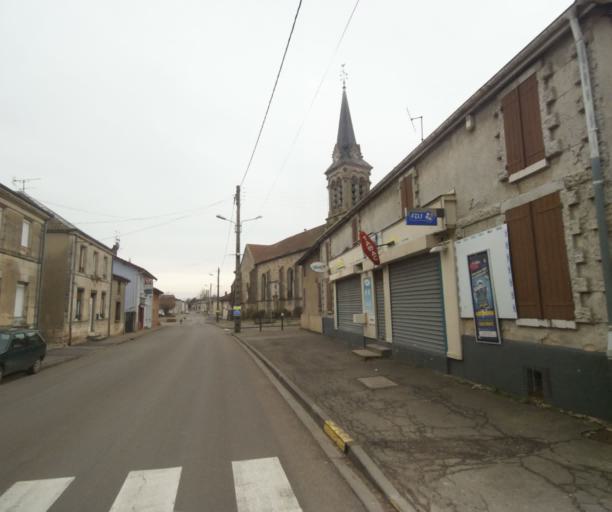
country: FR
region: Champagne-Ardenne
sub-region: Departement de la Haute-Marne
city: Villiers-en-Lieu
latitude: 48.6667
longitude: 4.8998
